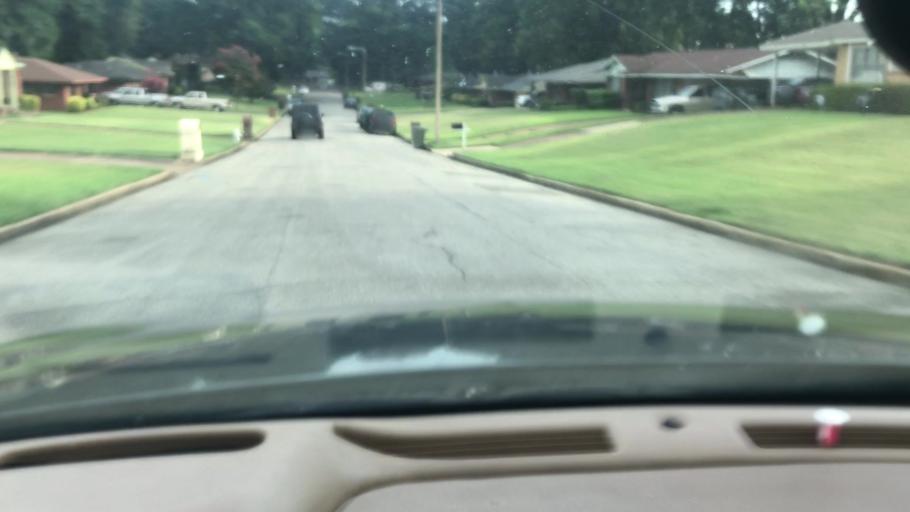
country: US
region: Tennessee
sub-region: Shelby County
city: New South Memphis
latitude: 35.0460
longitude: -90.0169
